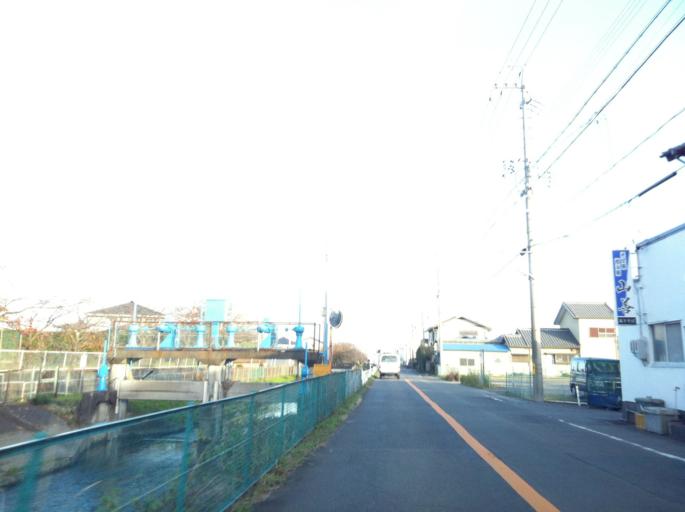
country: JP
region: Shizuoka
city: Fujieda
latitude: 34.8417
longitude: 138.2744
